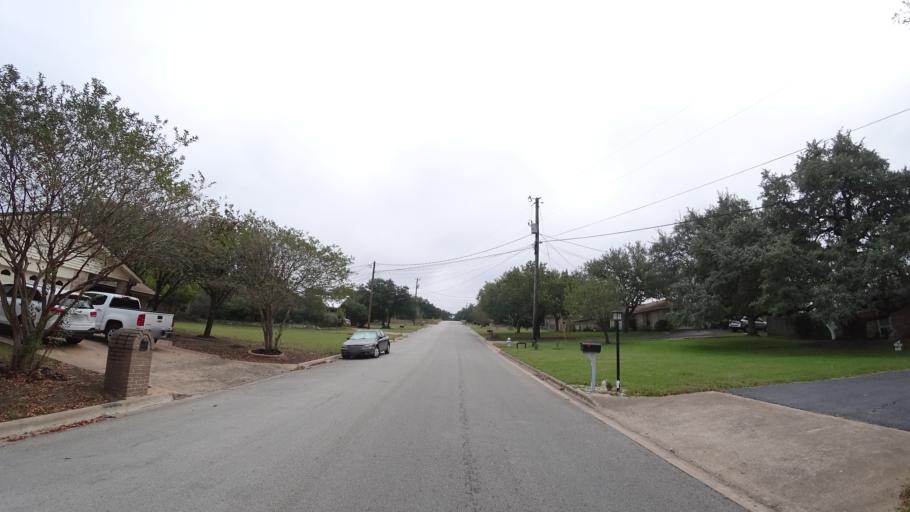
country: US
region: Texas
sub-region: Travis County
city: Shady Hollow
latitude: 30.2194
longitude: -97.8987
